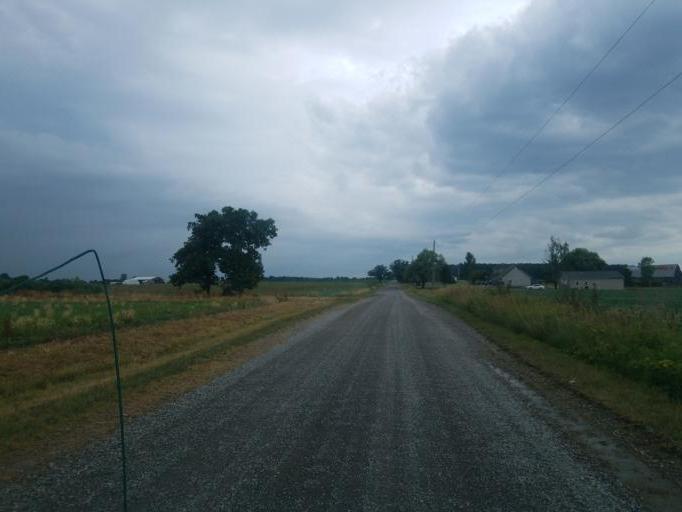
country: US
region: Ohio
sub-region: Defiance County
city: Hicksville
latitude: 41.3213
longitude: -84.8039
